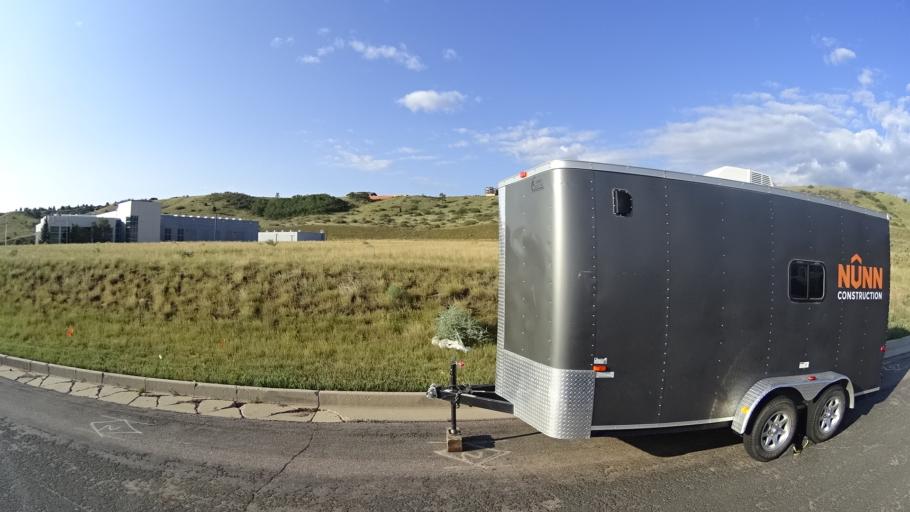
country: US
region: Colorado
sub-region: El Paso County
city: Manitou Springs
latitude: 38.8958
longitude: -104.8704
